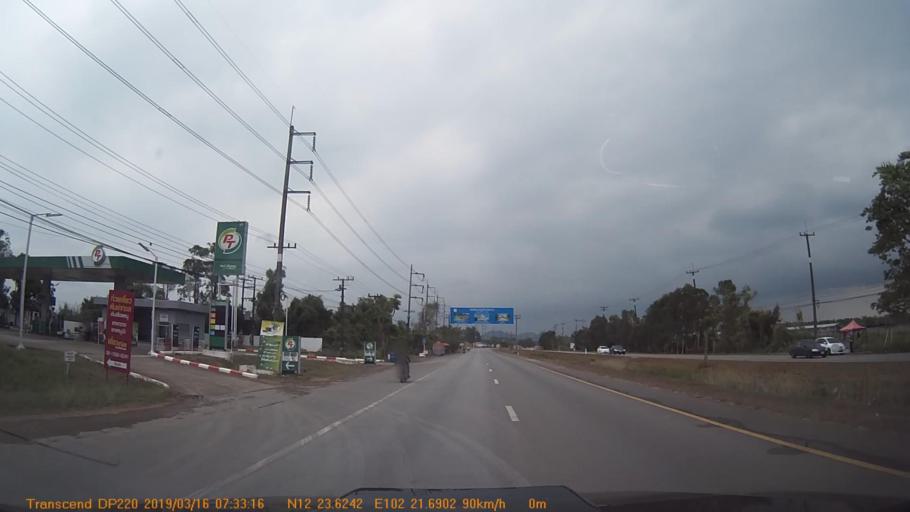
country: TH
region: Trat
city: Khao Saming
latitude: 12.3852
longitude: 102.3716
